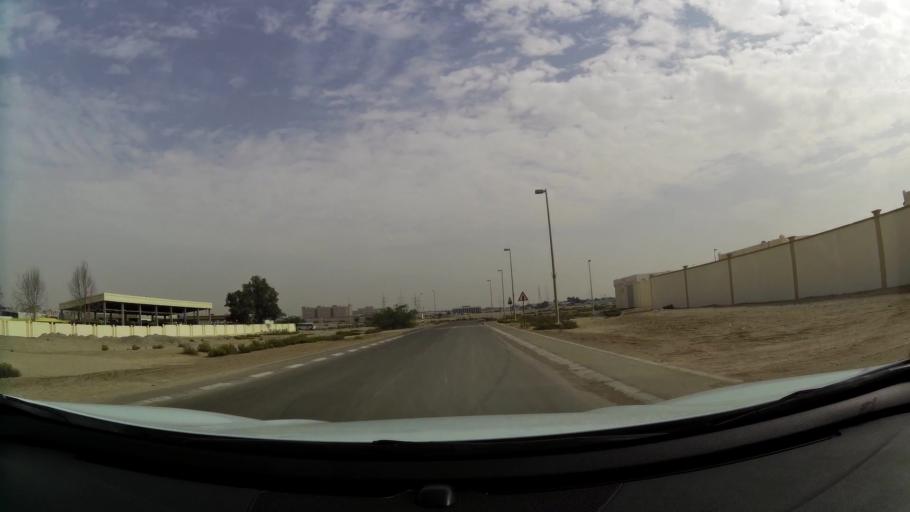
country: AE
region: Abu Dhabi
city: Abu Dhabi
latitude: 24.2871
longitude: 54.6574
